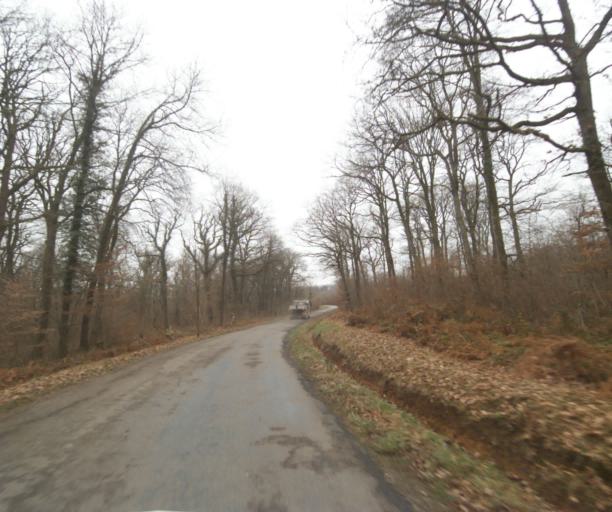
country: FR
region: Champagne-Ardenne
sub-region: Departement de la Haute-Marne
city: Wassy
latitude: 48.5218
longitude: 4.9745
